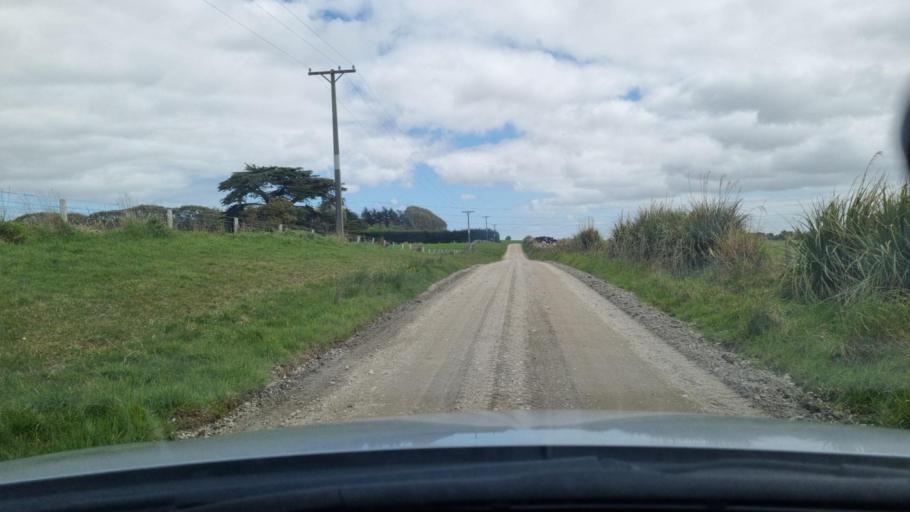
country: NZ
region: Southland
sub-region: Invercargill City
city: Invercargill
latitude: -46.4559
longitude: 168.4534
